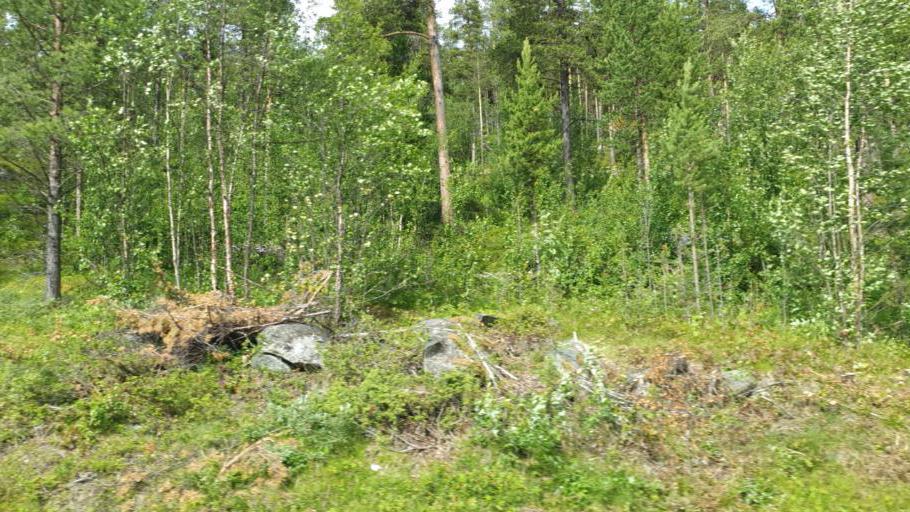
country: NO
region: Oppland
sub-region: Vaga
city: Vagamo
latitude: 61.6770
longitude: 9.0472
